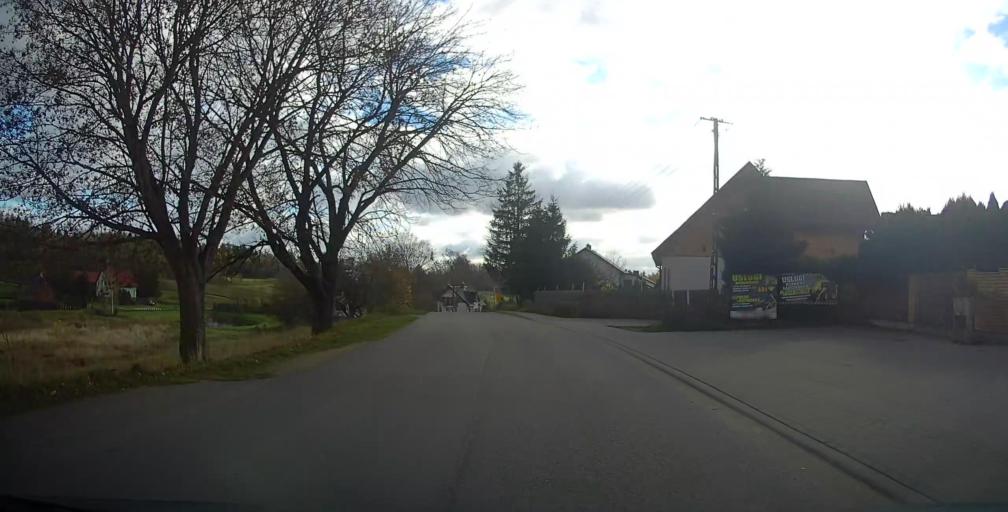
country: PL
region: Podlasie
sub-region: Suwalki
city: Suwalki
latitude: 54.2907
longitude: 22.8793
